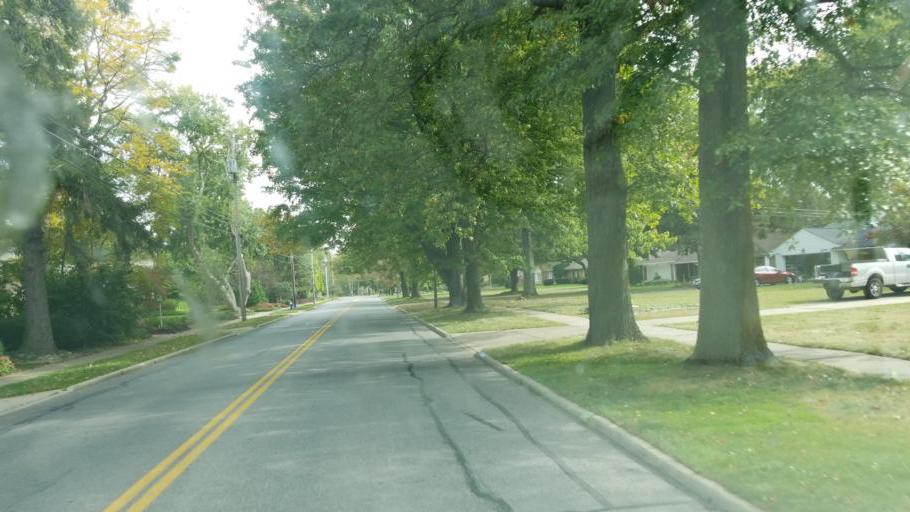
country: US
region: Ohio
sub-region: Cuyahoga County
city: Bay Village
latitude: 41.4963
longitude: -81.9568
